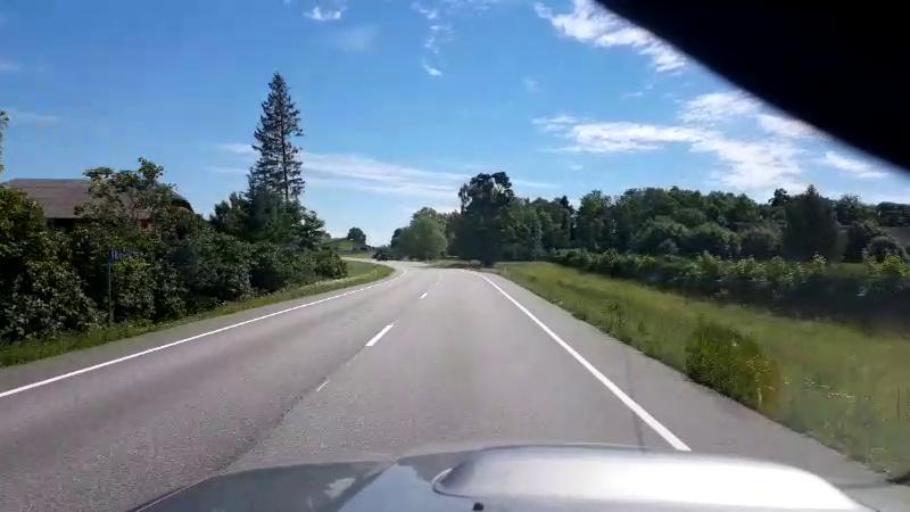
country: EE
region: Jaervamaa
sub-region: Jaerva-Jaani vald
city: Jarva-Jaani
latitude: 59.0038
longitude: 25.9312
